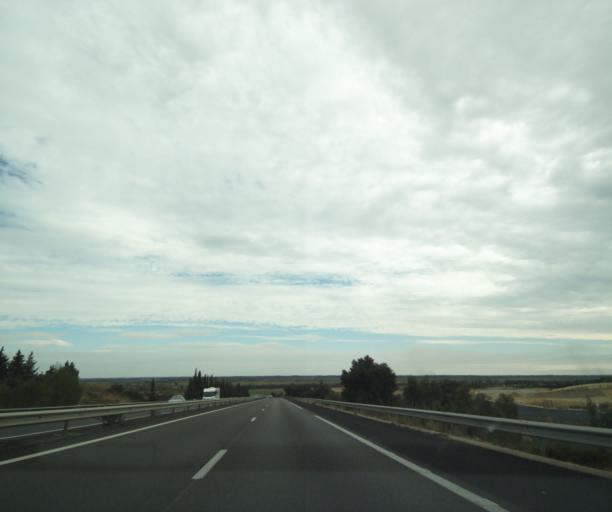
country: FR
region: Languedoc-Roussillon
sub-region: Departement du Gard
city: Garons
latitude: 43.7373
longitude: 4.4617
